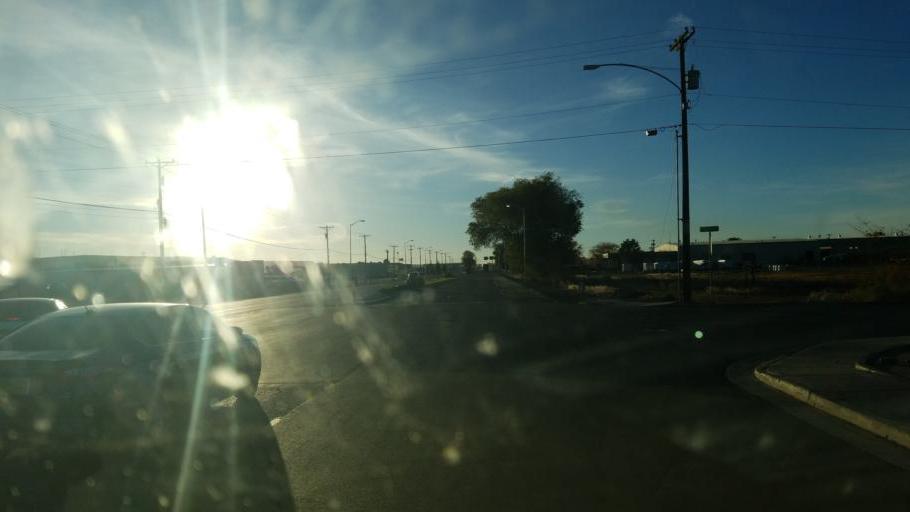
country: US
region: New Mexico
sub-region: San Juan County
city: Farmington
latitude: 36.7194
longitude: -108.1754
